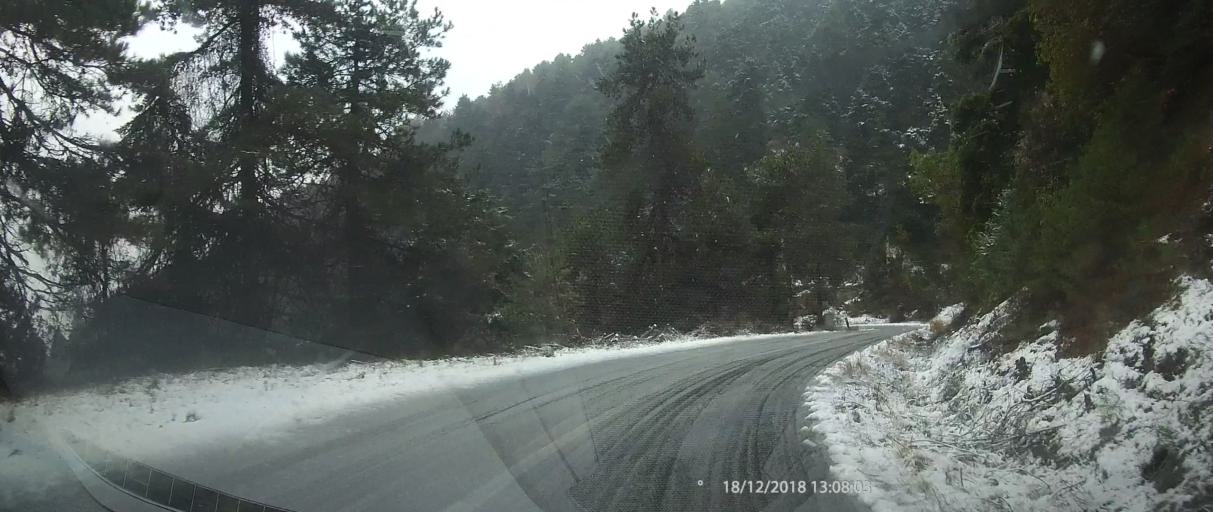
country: GR
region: Central Macedonia
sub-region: Nomos Pierias
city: Litochoro
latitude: 40.1067
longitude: 22.4756
